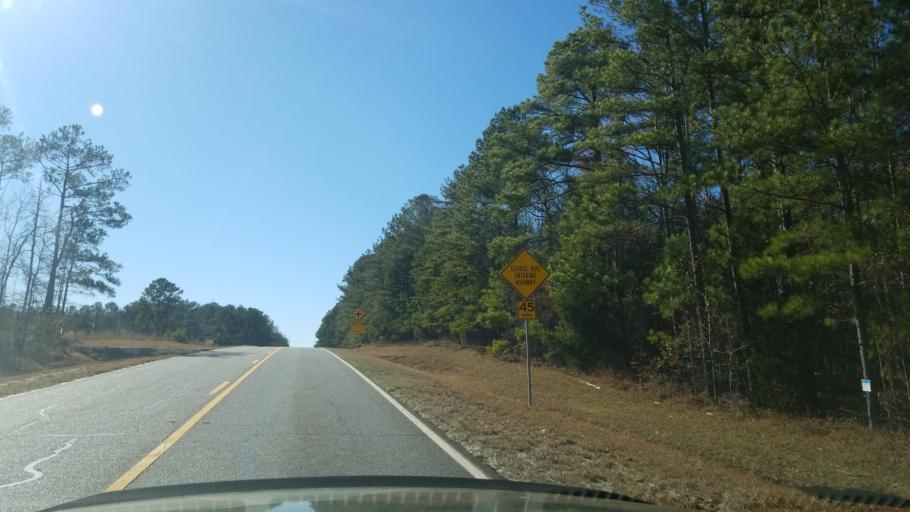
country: US
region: Georgia
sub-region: Talbot County
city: Sardis
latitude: 32.7899
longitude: -84.6775
